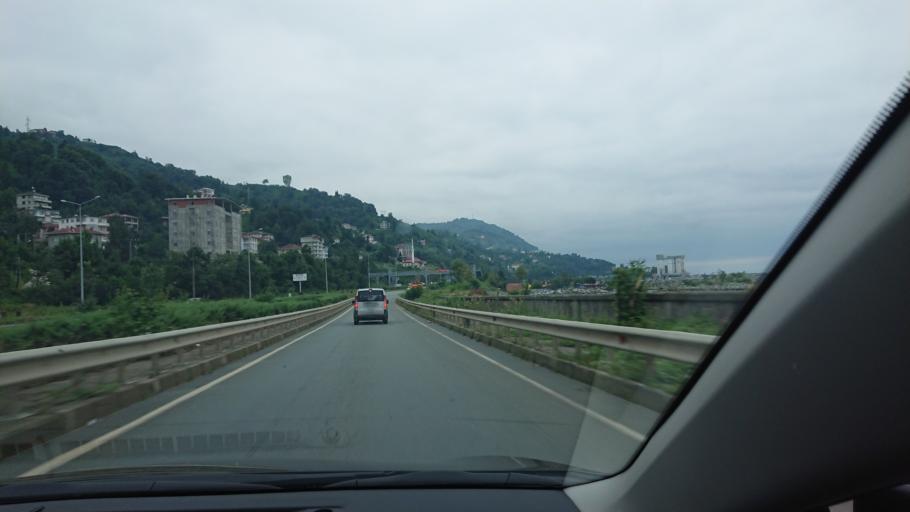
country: TR
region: Rize
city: Cayeli
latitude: 41.0810
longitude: 40.7014
